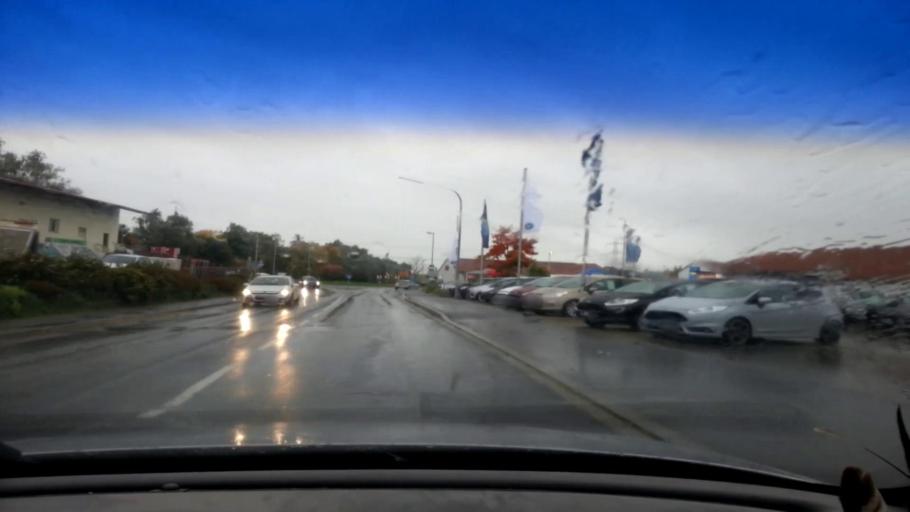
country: DE
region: Bavaria
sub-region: Upper Franconia
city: Schesslitz
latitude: 49.9705
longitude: 11.0255
